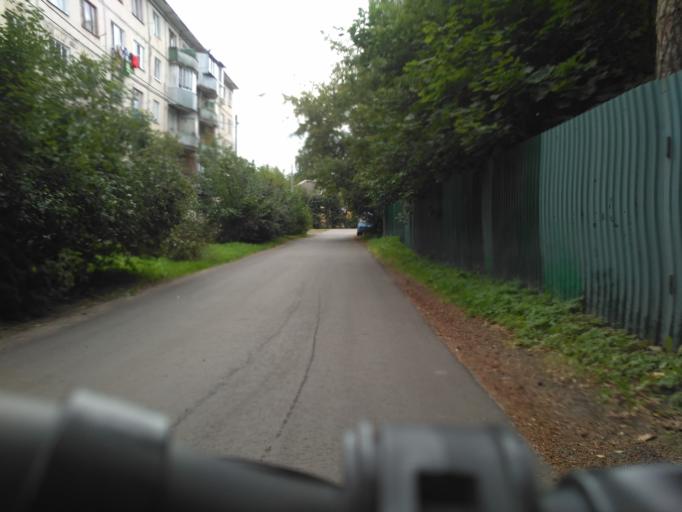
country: RU
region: Moskovskaya
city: Dubna
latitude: 56.7328
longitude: 37.1446
